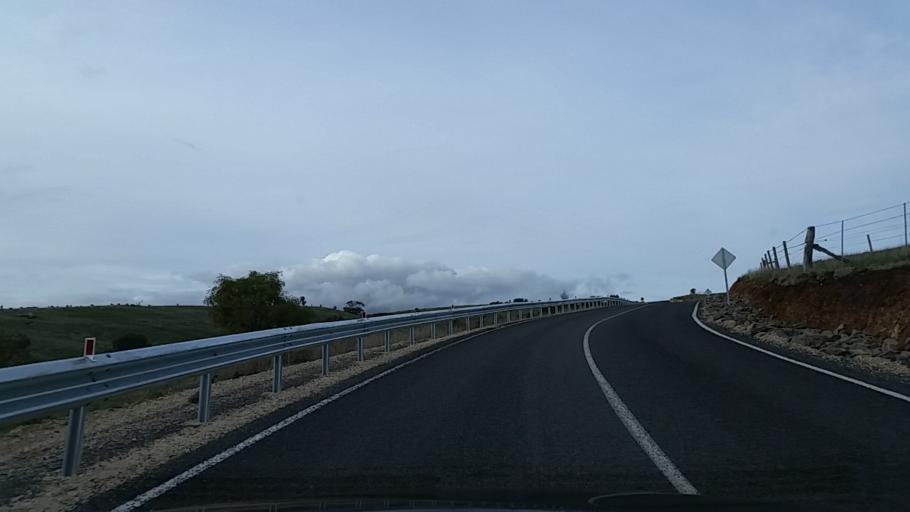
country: AU
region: South Australia
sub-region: Mount Barker
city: Callington
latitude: -35.0149
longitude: 139.0540
